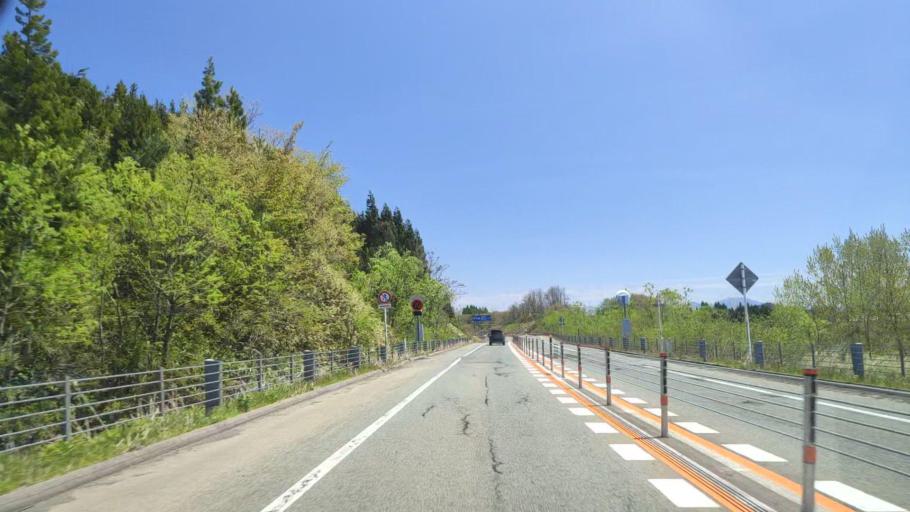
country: JP
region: Yamagata
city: Shinjo
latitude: 38.6718
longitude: 140.3296
